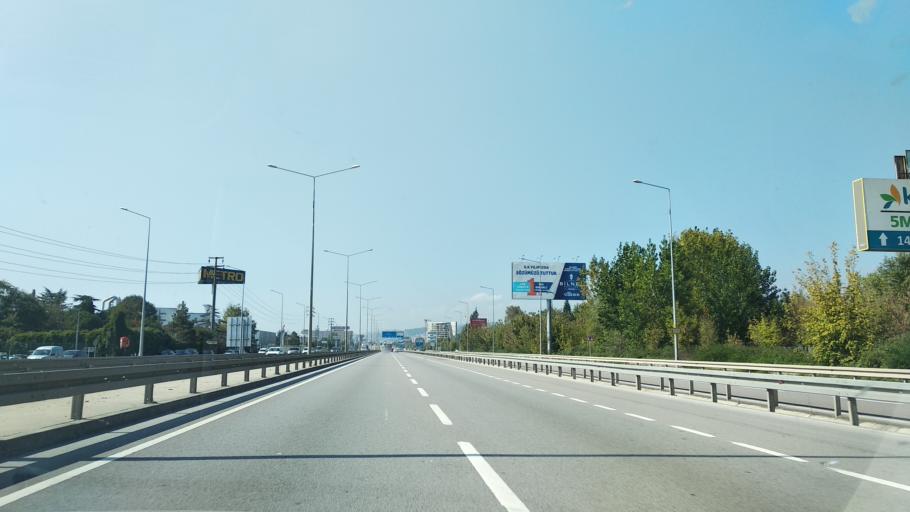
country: TR
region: Kocaeli
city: Kosekoy
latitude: 40.7572
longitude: 29.9976
